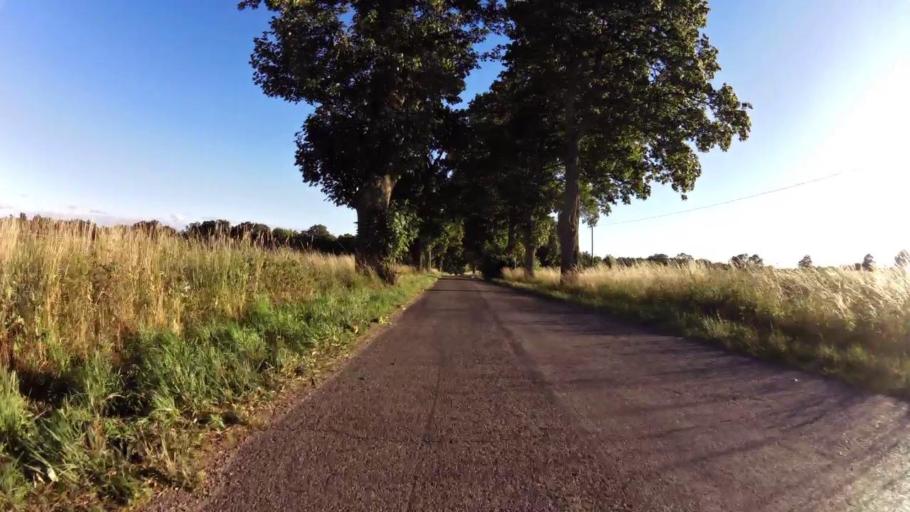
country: PL
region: West Pomeranian Voivodeship
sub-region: Powiat swidwinski
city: Swidwin
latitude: 53.7390
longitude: 15.6811
